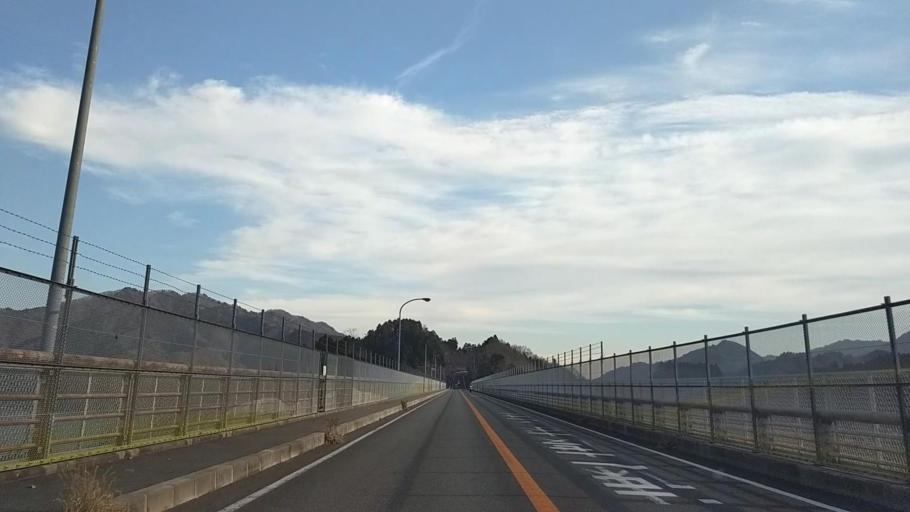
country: JP
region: Yamanashi
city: Uenohara
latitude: 35.5336
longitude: 139.2169
